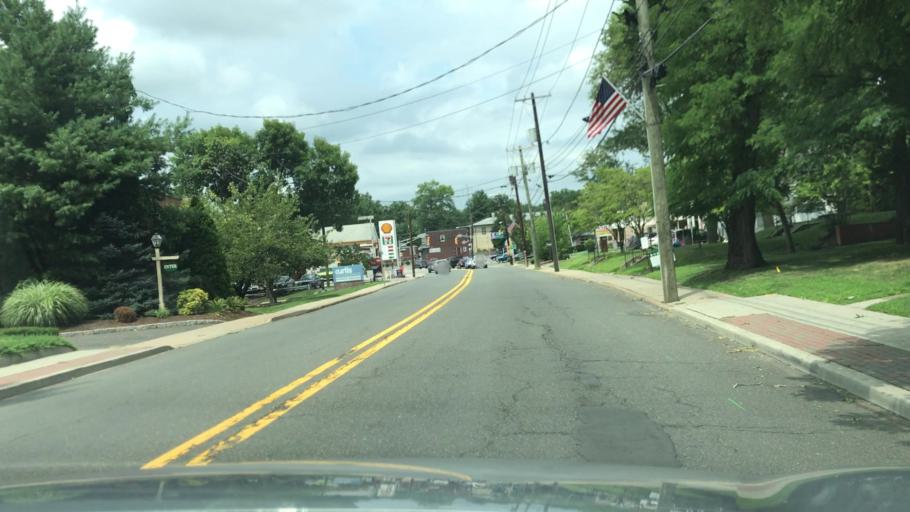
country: US
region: New Jersey
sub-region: Bergen County
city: New Milford
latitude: 40.9299
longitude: -74.0254
